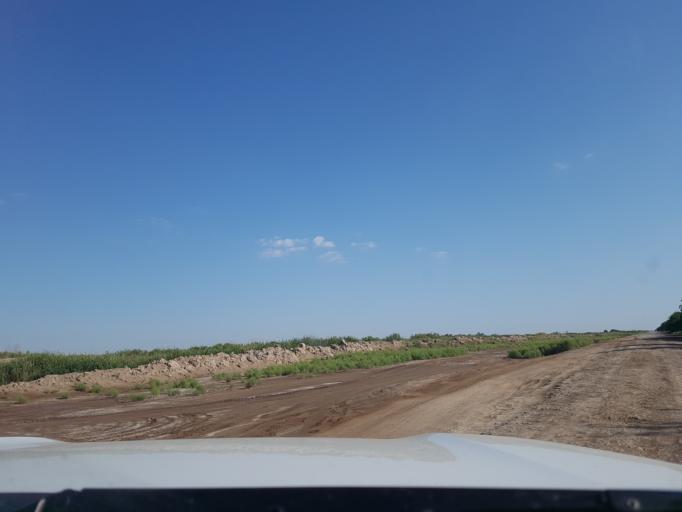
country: TM
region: Dasoguz
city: Koeneuergench
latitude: 41.9347
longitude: 58.7143
